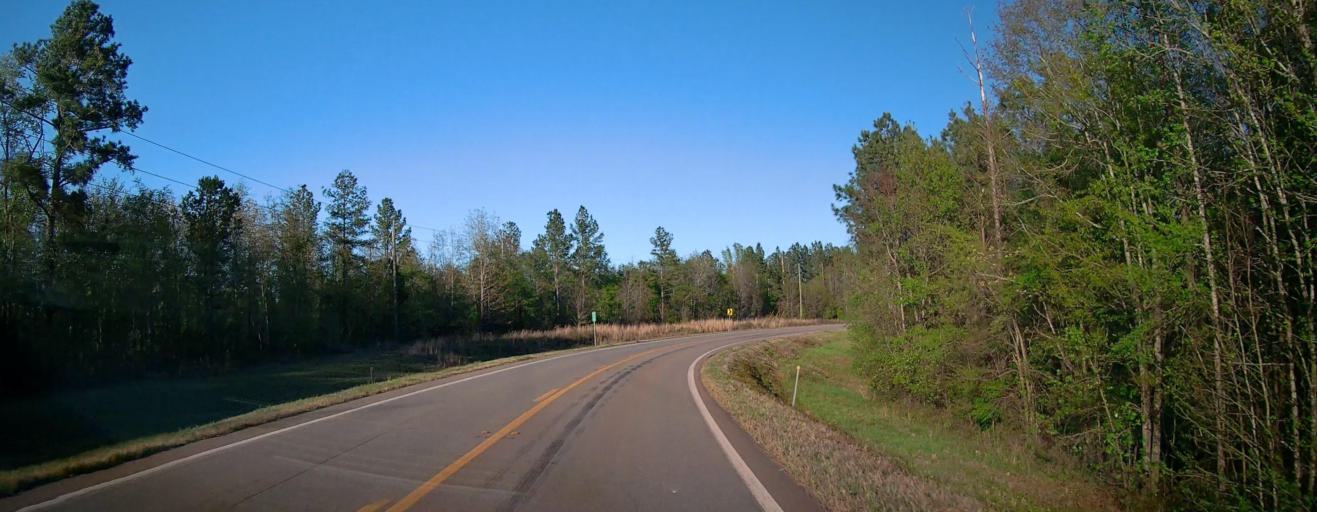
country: US
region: Georgia
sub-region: Wilkinson County
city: Irwinton
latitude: 32.8747
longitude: -83.1000
